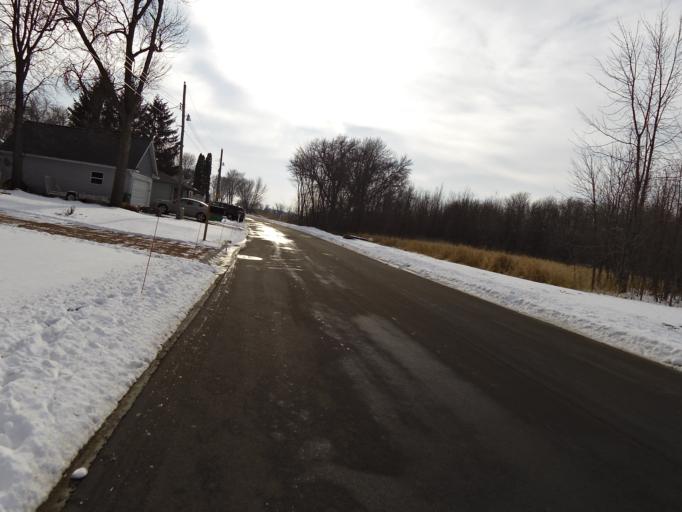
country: US
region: Minnesota
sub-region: Scott County
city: Prior Lake
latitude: 44.7012
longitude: -93.4885
